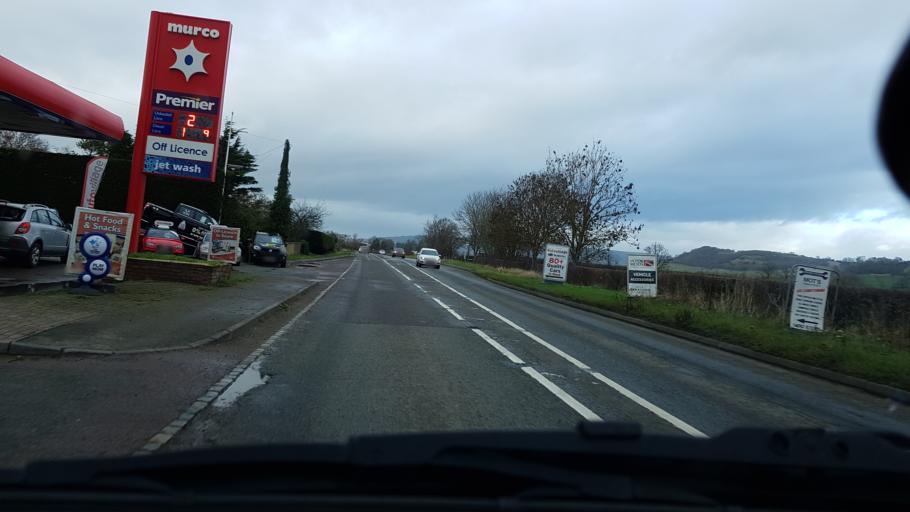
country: GB
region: England
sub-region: Gloucestershire
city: Gotherington
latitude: 51.9637
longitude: -2.0695
